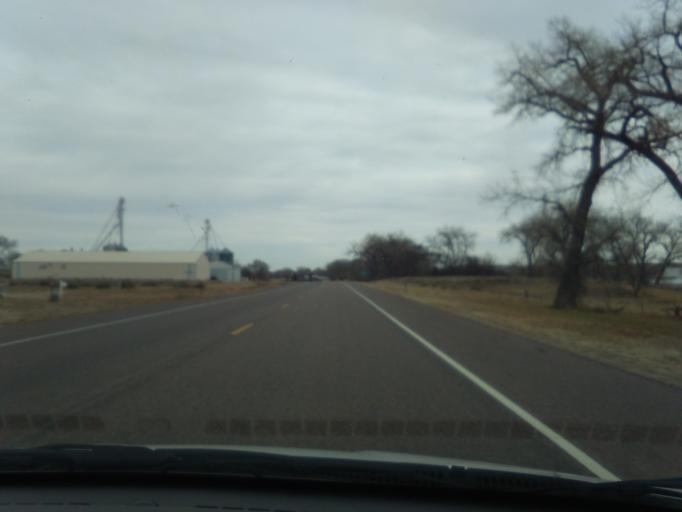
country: US
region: Colorado
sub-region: Yuma County
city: Wray
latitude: 40.0754
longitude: -102.2693
